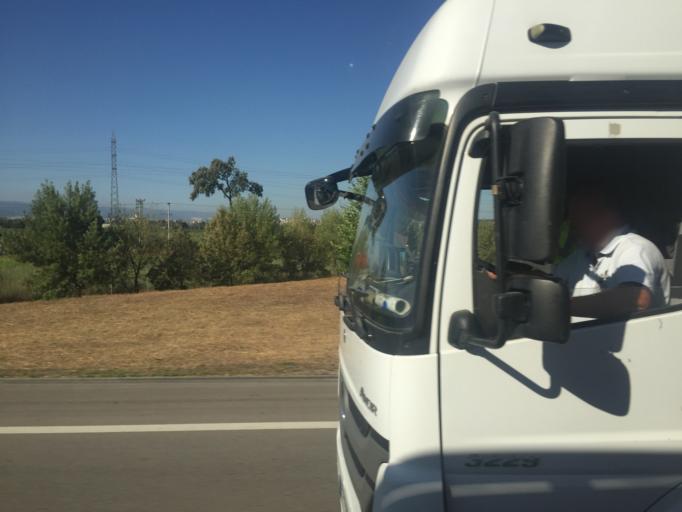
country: TR
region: Bursa
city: Demirtas
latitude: 40.2758
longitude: 29.0459
